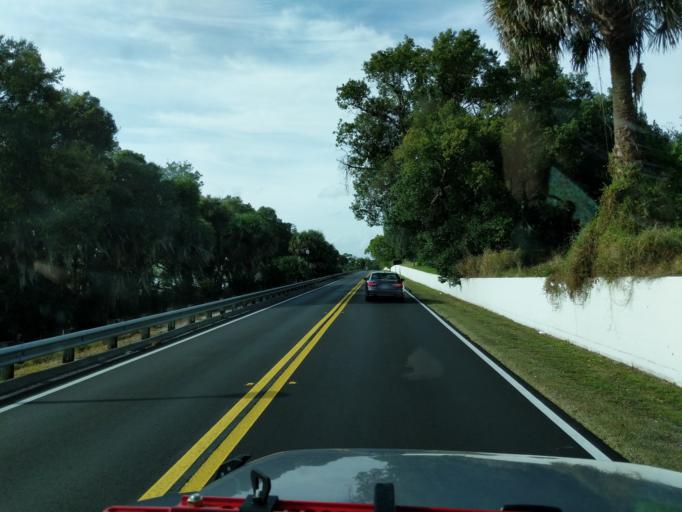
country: US
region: Florida
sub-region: Lake County
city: Mount Dora
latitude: 28.8040
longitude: -81.6515
